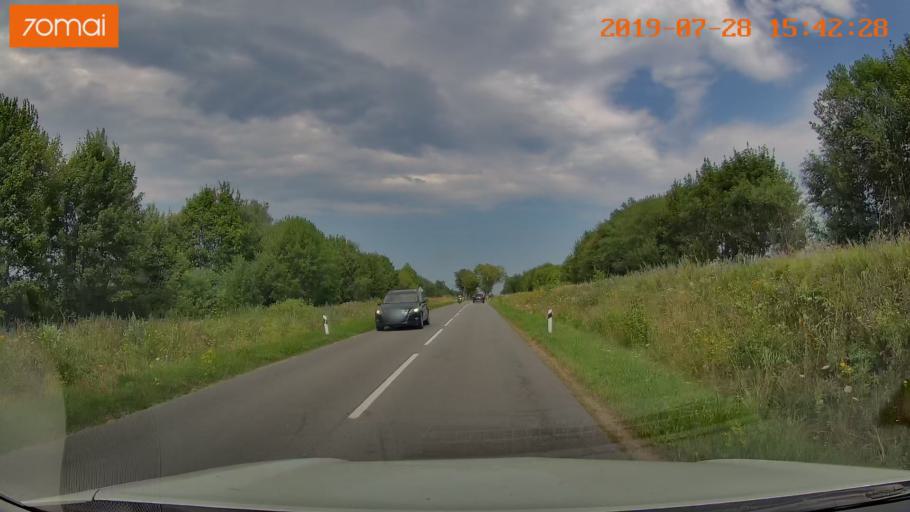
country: RU
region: Kaliningrad
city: Donskoye
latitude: 54.9309
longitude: 20.0113
